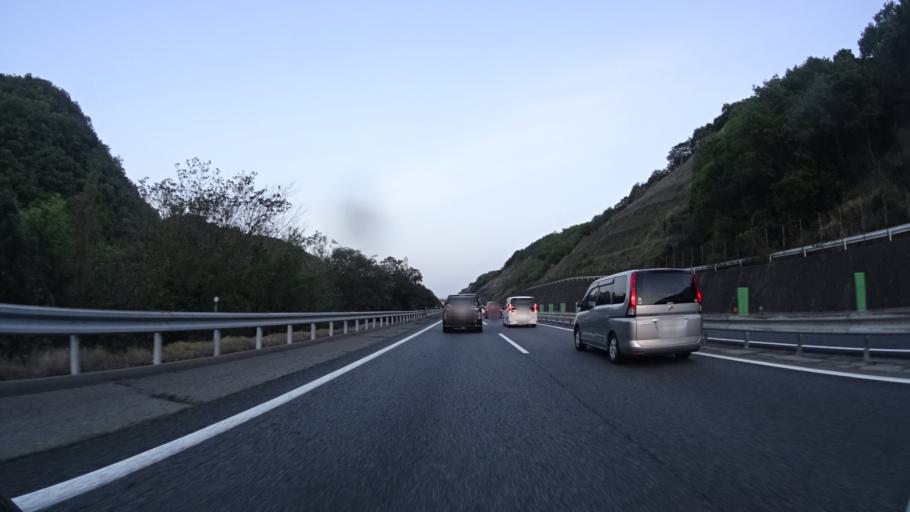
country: JP
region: Hyogo
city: Kariya
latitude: 34.7799
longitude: 134.2293
